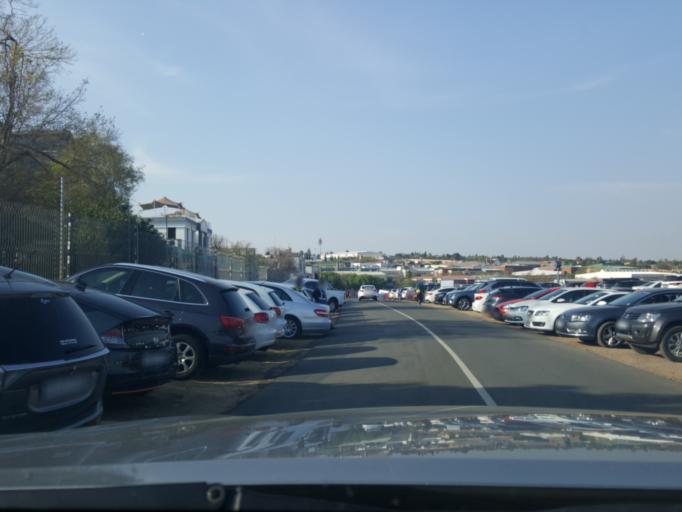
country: ZA
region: Gauteng
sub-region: City of Johannesburg Metropolitan Municipality
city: Midrand
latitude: -25.9952
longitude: 28.0698
